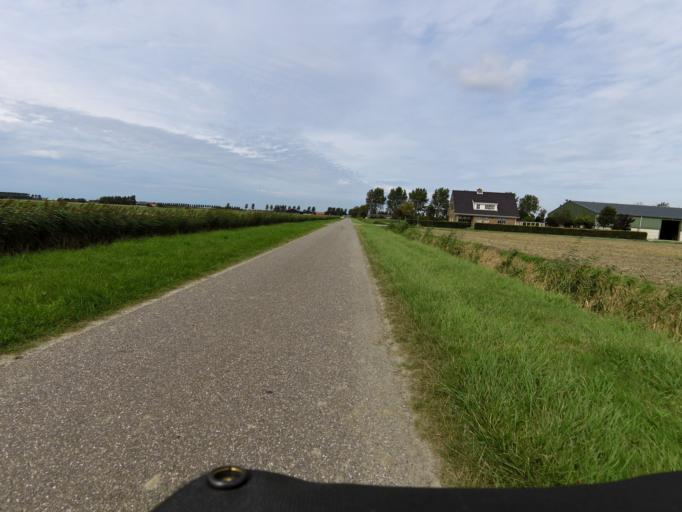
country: NL
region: South Holland
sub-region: Gemeente Goeree-Overflakkee
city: Middelharnis
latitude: 51.6994
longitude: 4.1564
